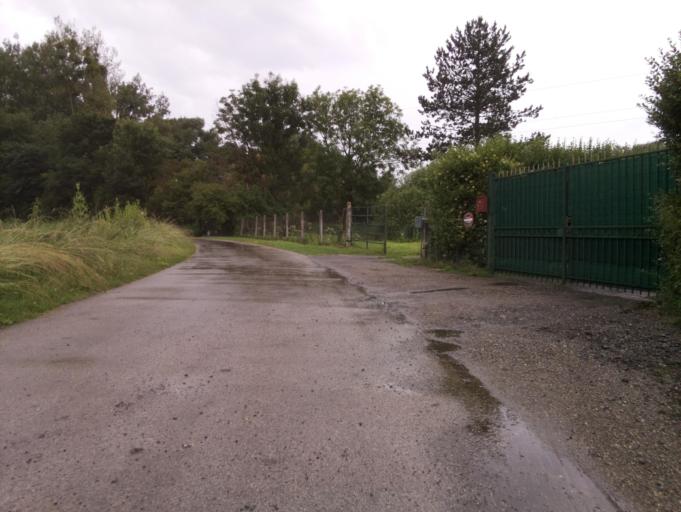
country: FR
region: Picardie
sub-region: Departement de la Somme
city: Ailly-sur-Somme
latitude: 49.9361
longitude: 2.1826
